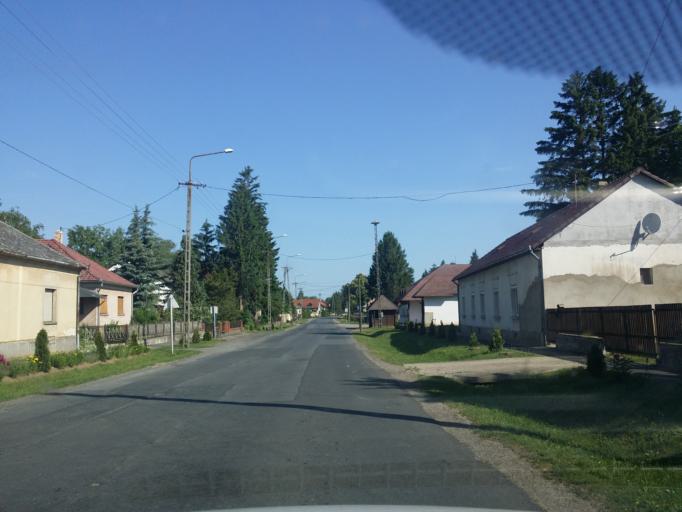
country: HU
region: Zala
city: Zalaszentgrot
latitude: 46.8753
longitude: 17.1125
